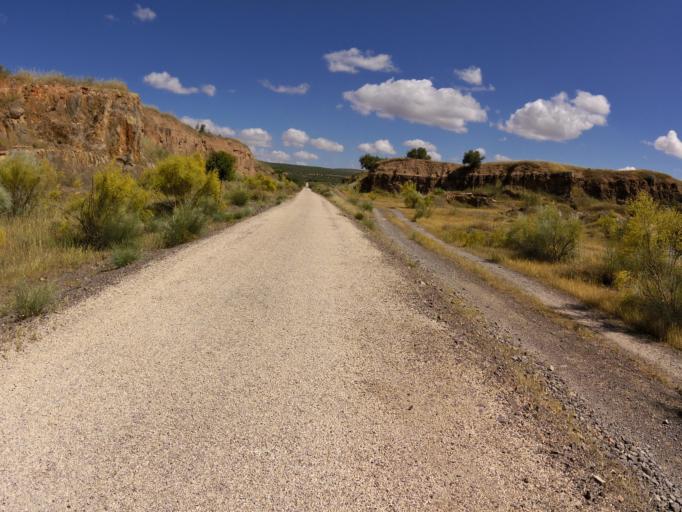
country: ES
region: Andalusia
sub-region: Provincia de Jaen
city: Alcaudete
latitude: 37.6342
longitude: -4.0827
